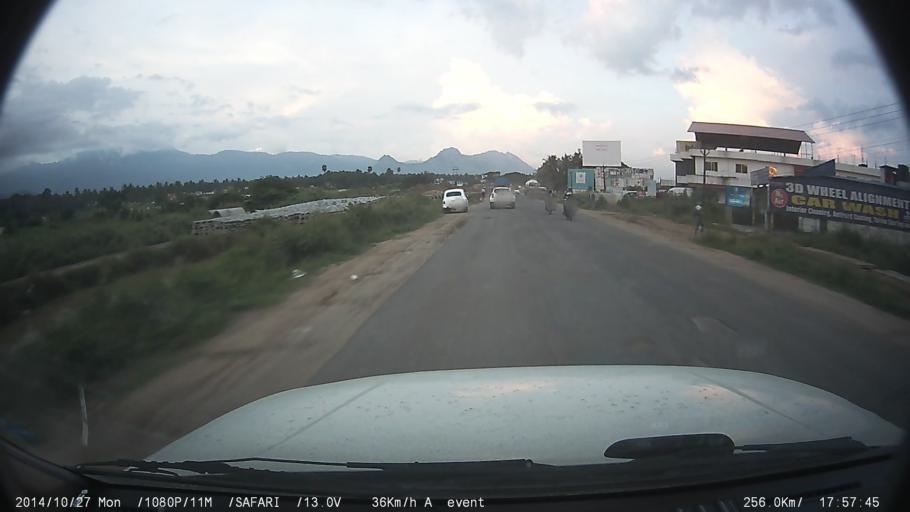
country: IN
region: Kerala
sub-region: Palakkad district
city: Palakkad
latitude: 10.7616
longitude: 76.6718
